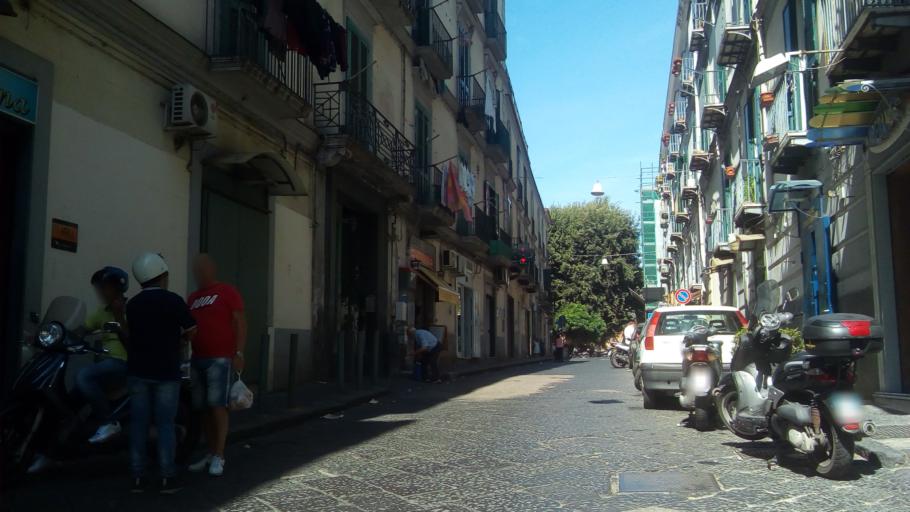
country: IT
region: Campania
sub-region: Provincia di Napoli
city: Napoli
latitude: 40.8656
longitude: 14.2534
